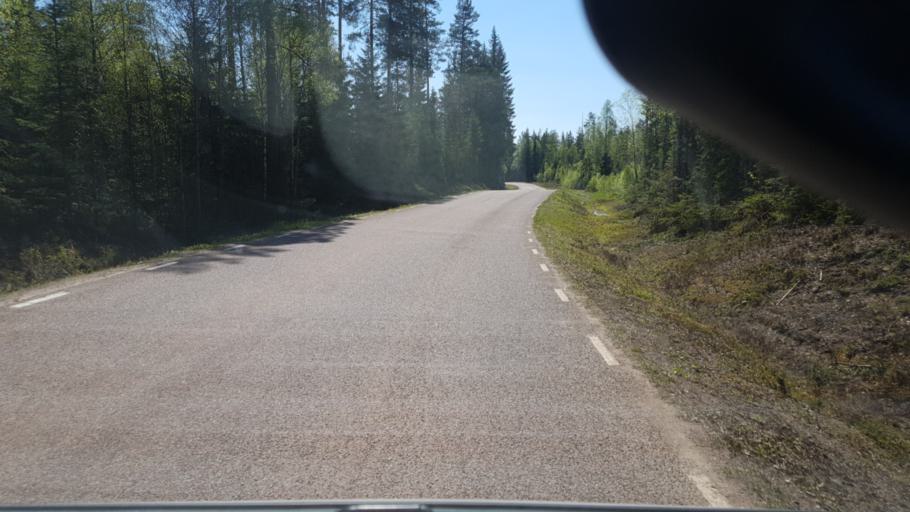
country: SE
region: Vaermland
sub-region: Arvika Kommun
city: Arvika
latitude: 59.8014
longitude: 12.8373
